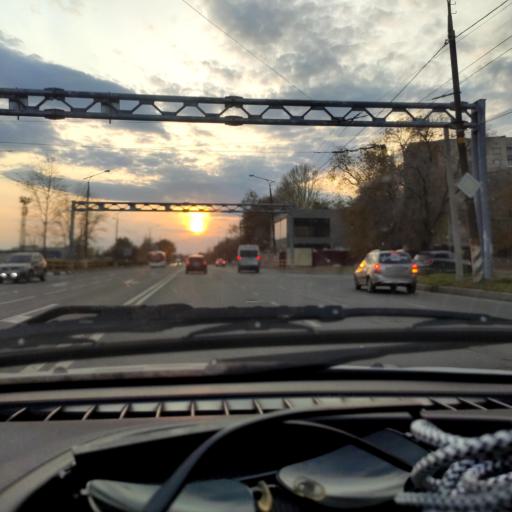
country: RU
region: Samara
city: Zhigulevsk
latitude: 53.4760
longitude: 49.4857
